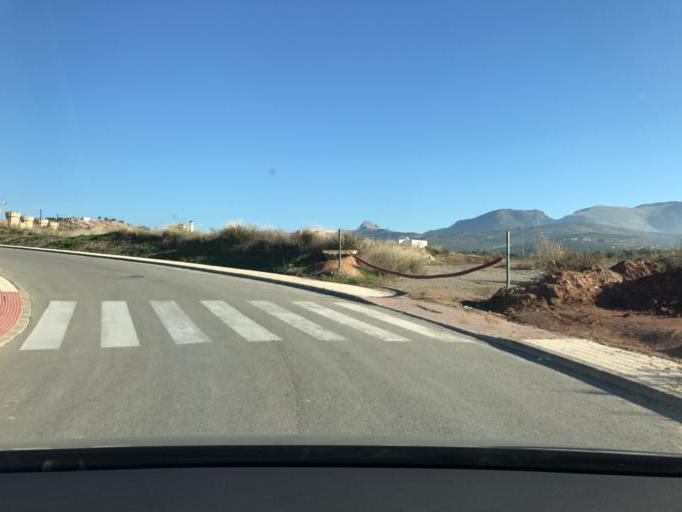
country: ES
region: Andalusia
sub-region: Provincia de Granada
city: Peligros
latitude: 37.2351
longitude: -3.6159
